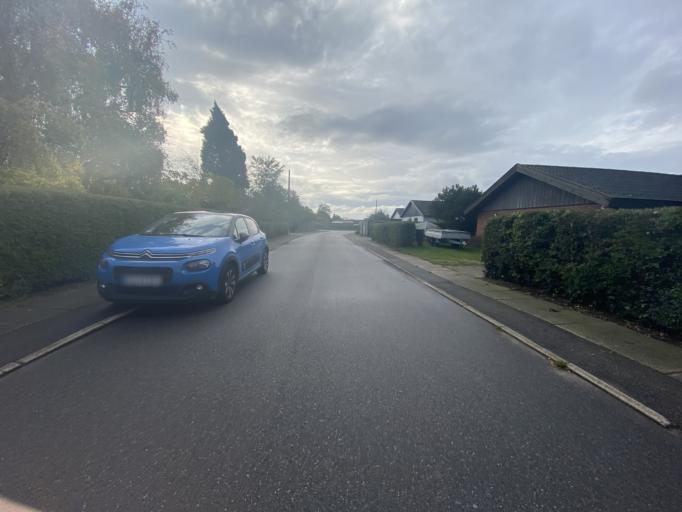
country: DK
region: Capital Region
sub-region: Dragor Kommune
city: Dragor
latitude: 55.5881
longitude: 12.6479
